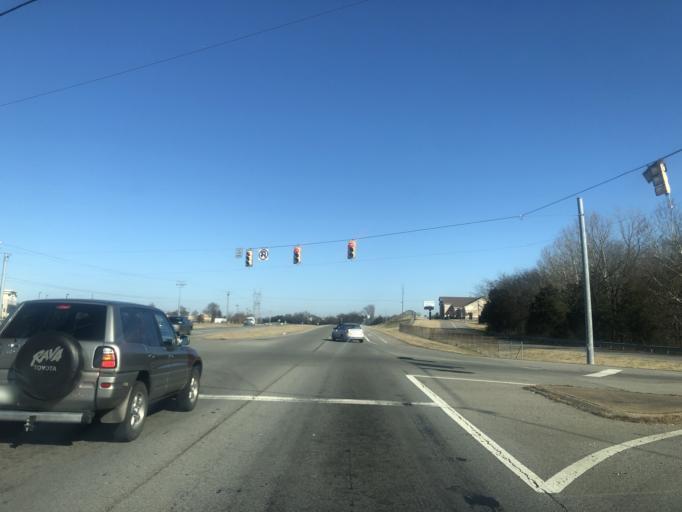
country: US
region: Tennessee
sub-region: Rutherford County
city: Smyrna
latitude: 35.9379
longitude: -86.5289
